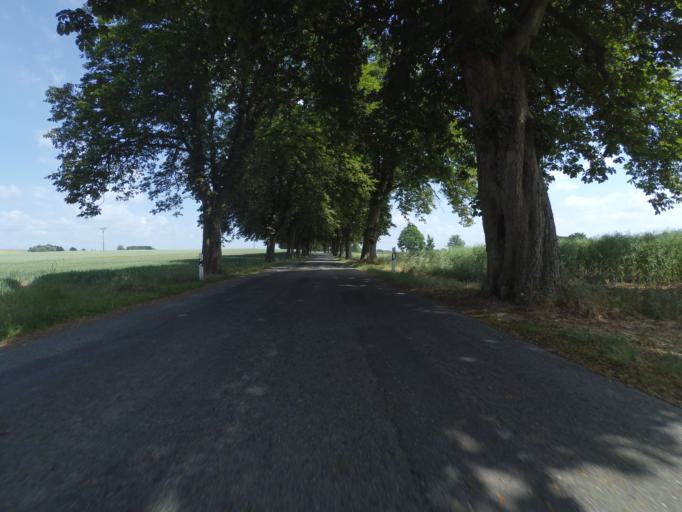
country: DE
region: Mecklenburg-Vorpommern
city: Lubz
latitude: 53.4453
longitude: 12.0684
